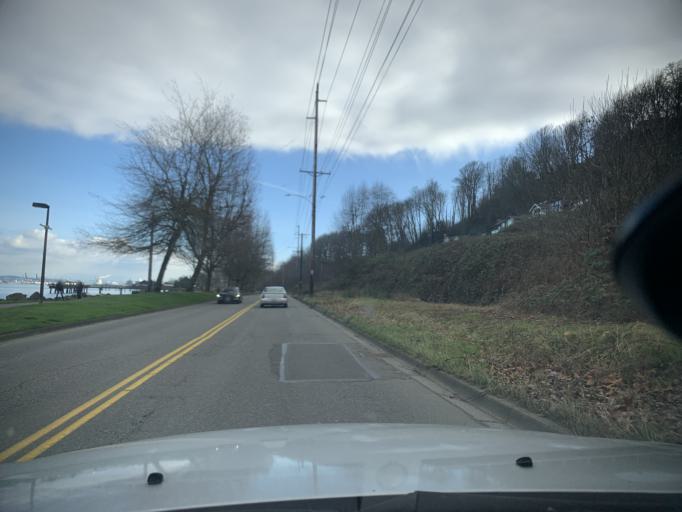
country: US
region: Washington
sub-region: Pierce County
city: Tacoma
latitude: 47.2848
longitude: -122.4858
